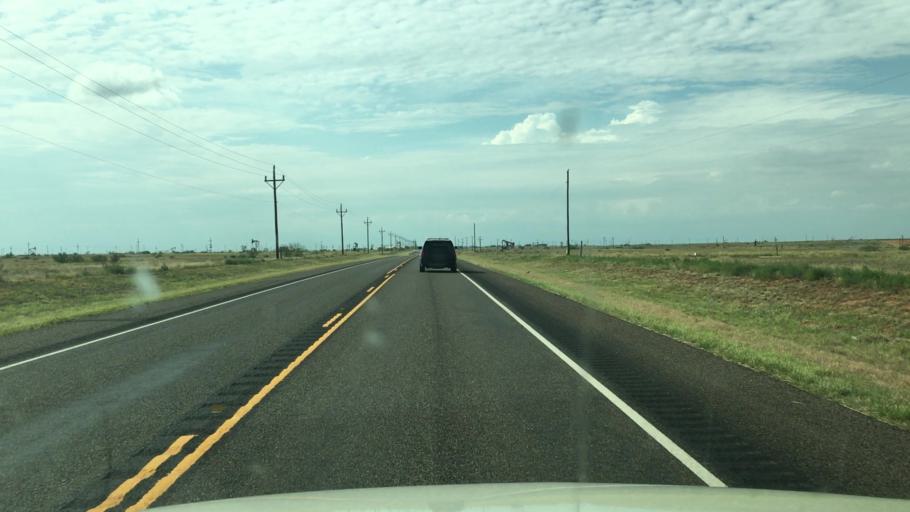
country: US
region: Texas
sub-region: Dawson County
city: Lamesa
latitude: 32.8915
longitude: -102.0909
